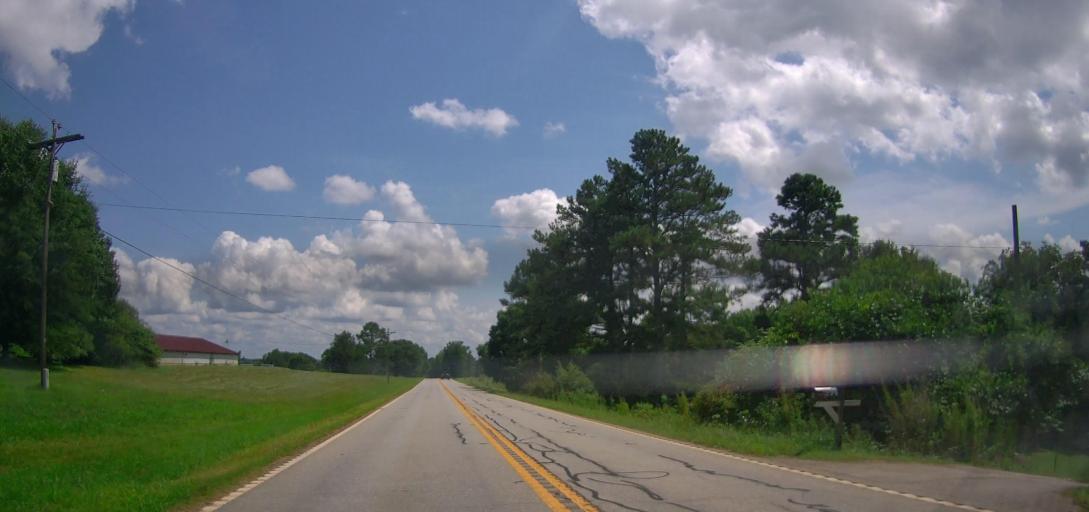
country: US
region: Georgia
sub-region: Carroll County
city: Bowdon
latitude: 33.4245
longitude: -85.2675
